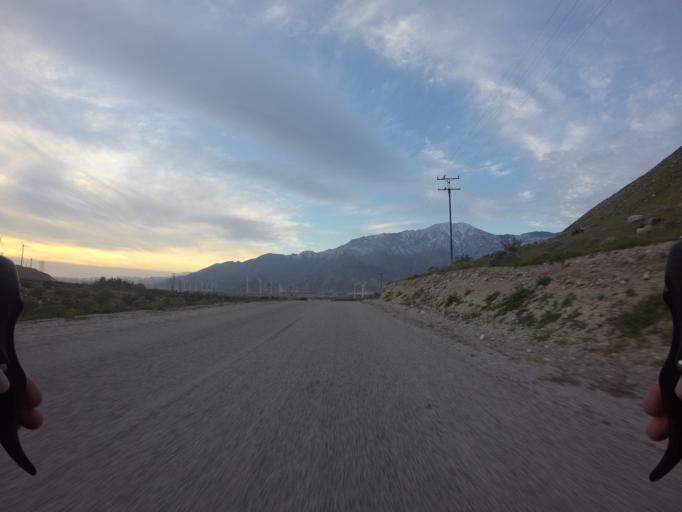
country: US
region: California
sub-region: Riverside County
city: Garnet
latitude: 33.9280
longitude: -116.6420
